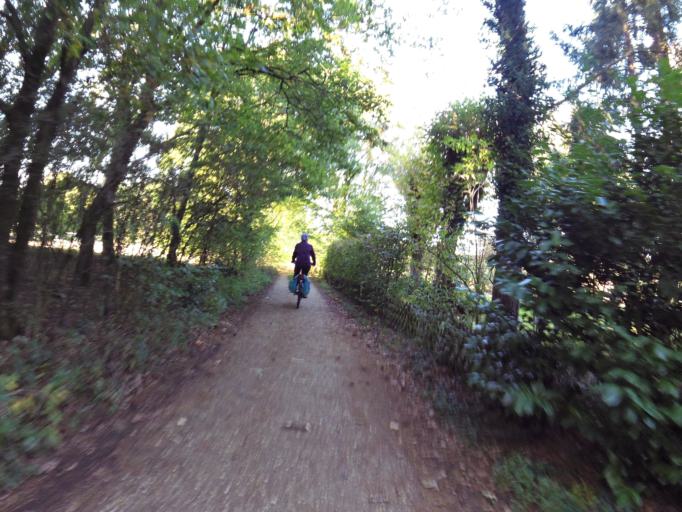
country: NL
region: Limburg
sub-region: Gemeente Bergen
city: Wellerlooi
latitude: 51.5280
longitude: 6.1484
